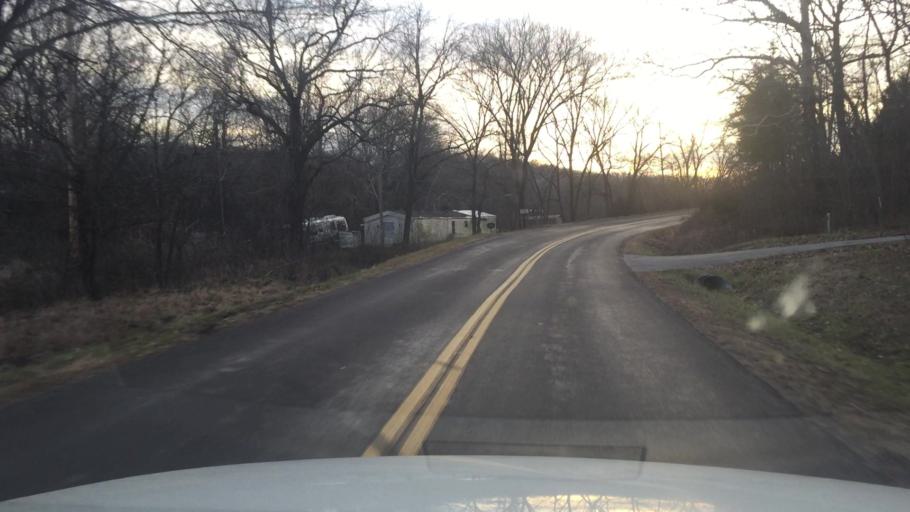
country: US
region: Missouri
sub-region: Miller County
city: Eldon
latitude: 38.3406
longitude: -92.7097
